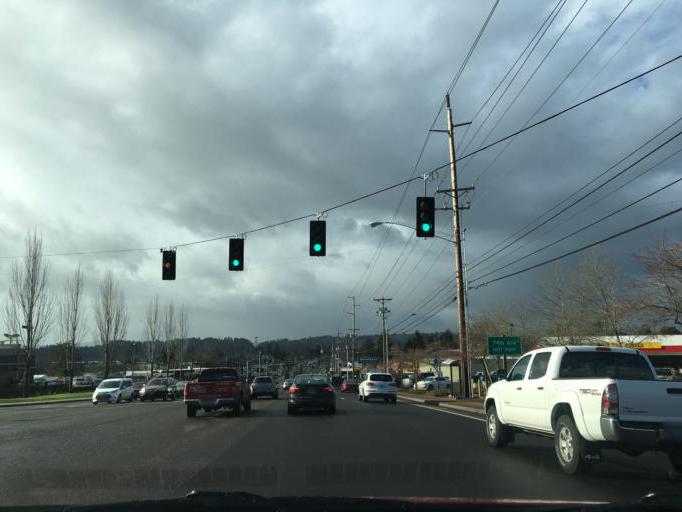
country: US
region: Oregon
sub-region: Washington County
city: Metzger
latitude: 45.4401
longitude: -122.7514
